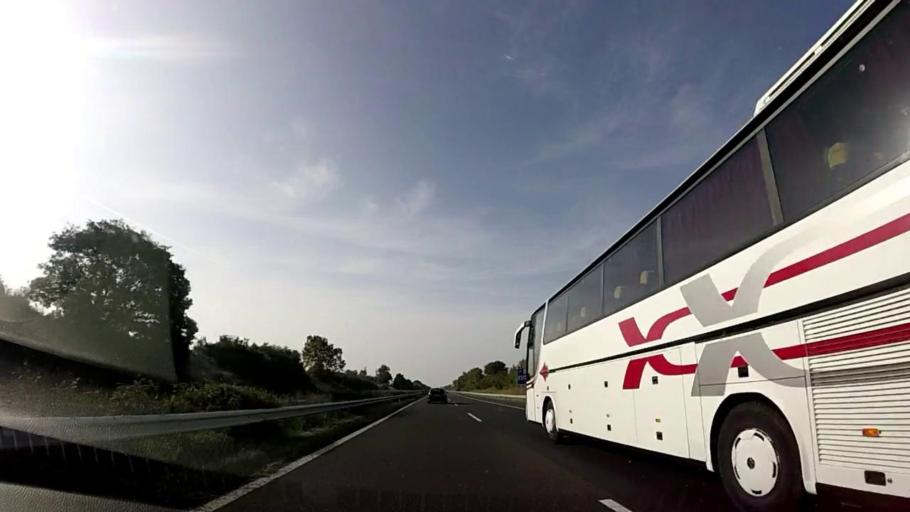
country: HU
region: Somogy
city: Balatonszabadi
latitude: 46.9683
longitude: 18.1659
